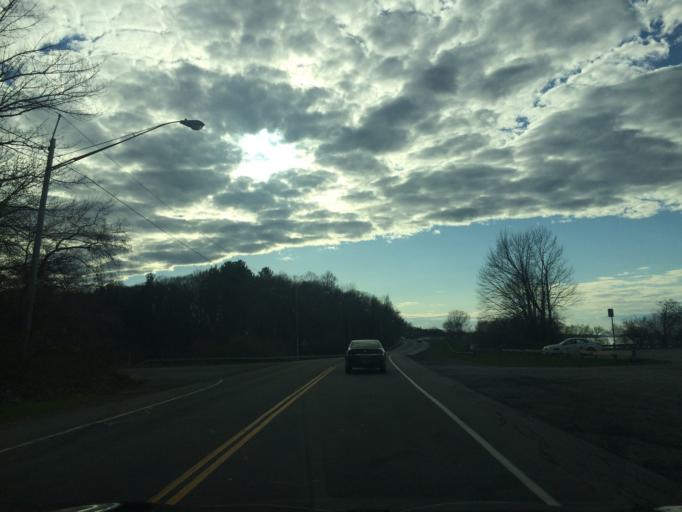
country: US
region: New York
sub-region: Monroe County
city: Irondequoit
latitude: 43.2362
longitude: -77.5571
